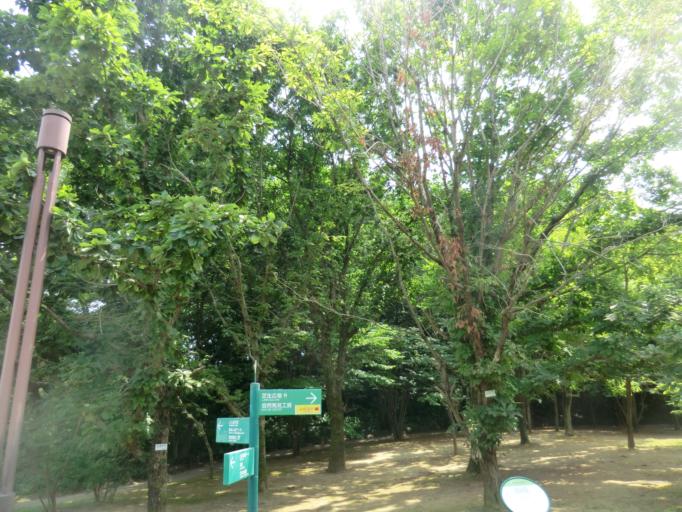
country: JP
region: Ibaraki
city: Iwai
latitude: 36.0044
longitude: 139.9156
